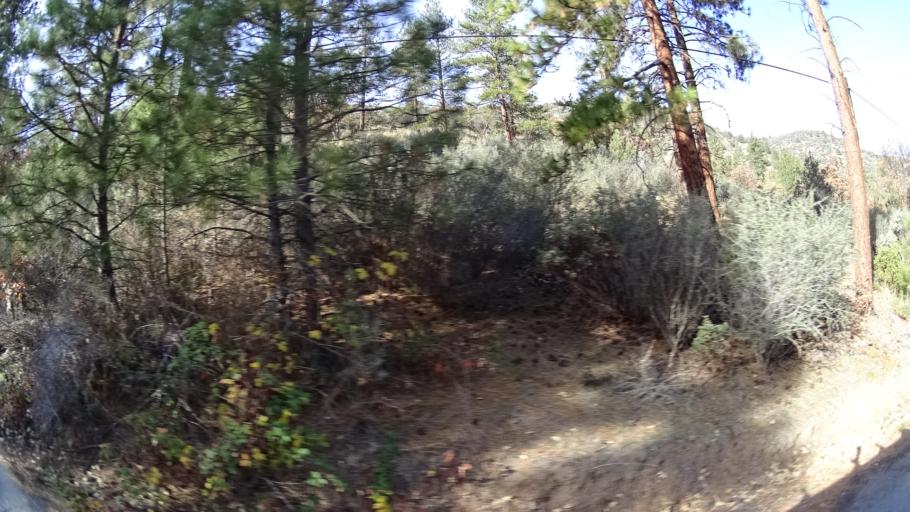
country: US
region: California
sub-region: Siskiyou County
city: Montague
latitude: 41.6089
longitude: -122.5773
